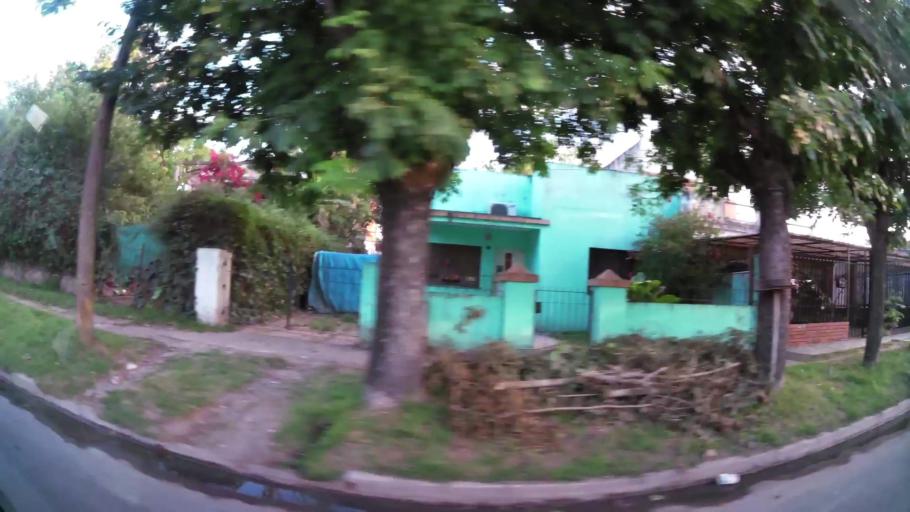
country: AR
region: Buenos Aires
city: Santa Catalina - Dique Lujan
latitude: -34.4726
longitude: -58.7598
